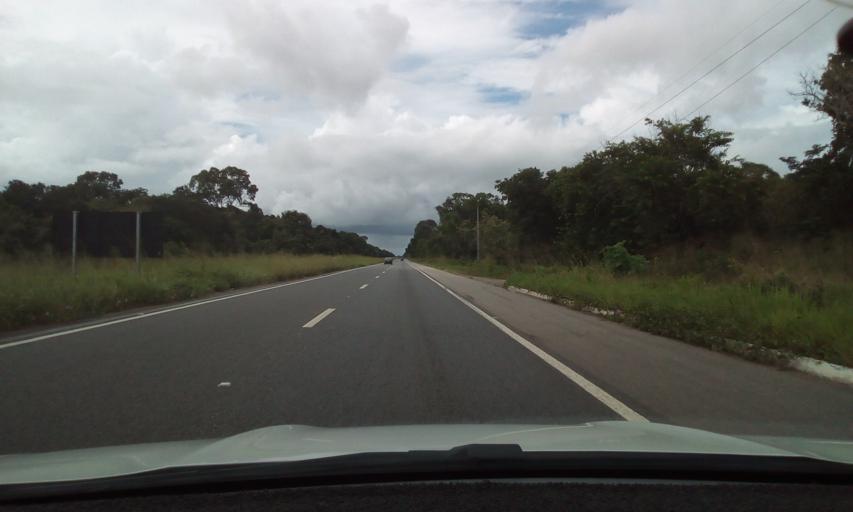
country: BR
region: Paraiba
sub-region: Cruz Do Espirito Santo
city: Cruz do Espirito Santo
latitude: -7.2025
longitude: -35.1066
